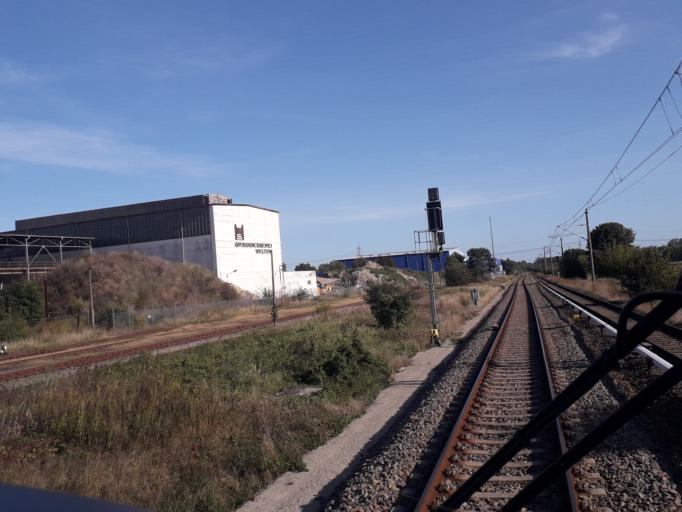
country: DE
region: Brandenburg
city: Velten
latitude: 52.6785
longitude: 13.1816
